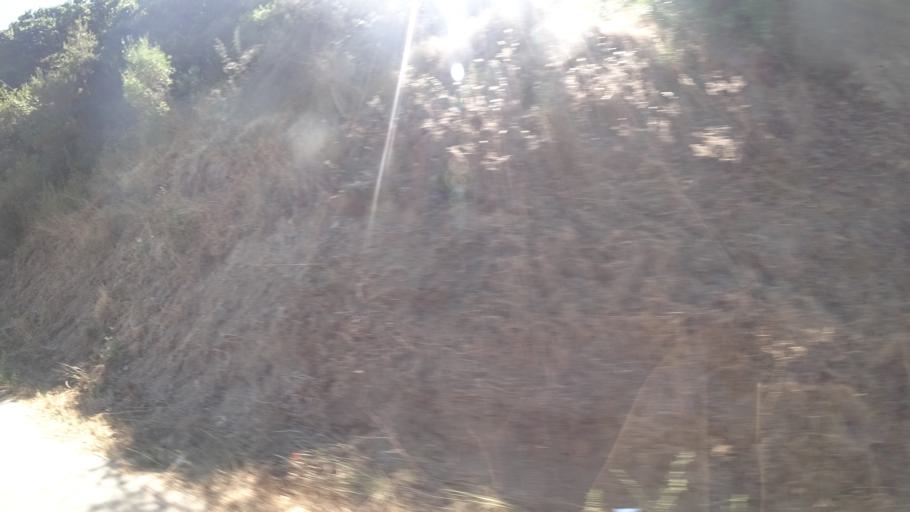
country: FR
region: Corsica
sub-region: Departement de la Corse-du-Sud
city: Alata
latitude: 41.9798
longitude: 8.6714
